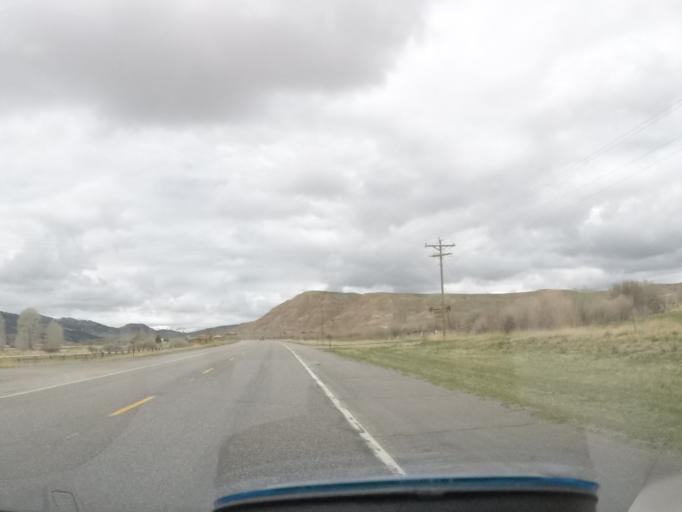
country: US
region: Wyoming
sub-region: Sublette County
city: Pinedale
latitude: 43.5650
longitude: -109.7035
